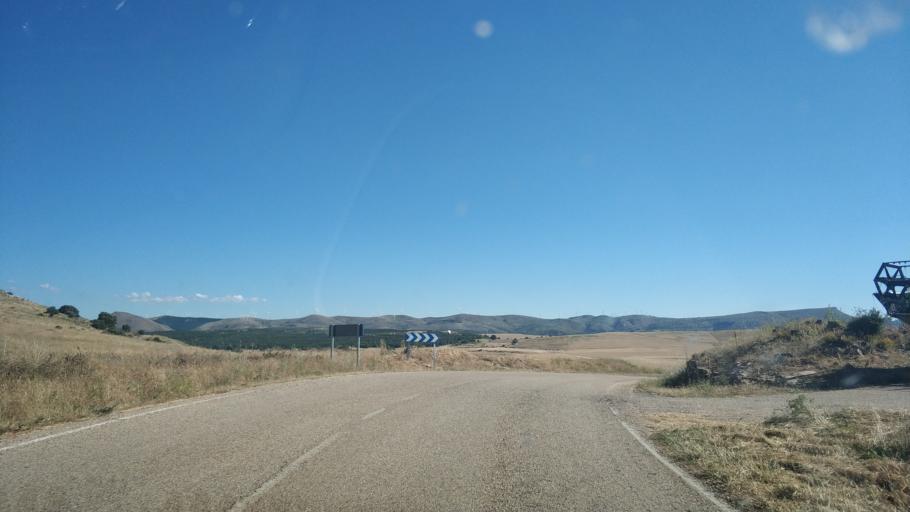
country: ES
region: Castille and Leon
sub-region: Provincia de Soria
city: Montejo de Tiermes
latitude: 41.3722
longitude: -3.1914
